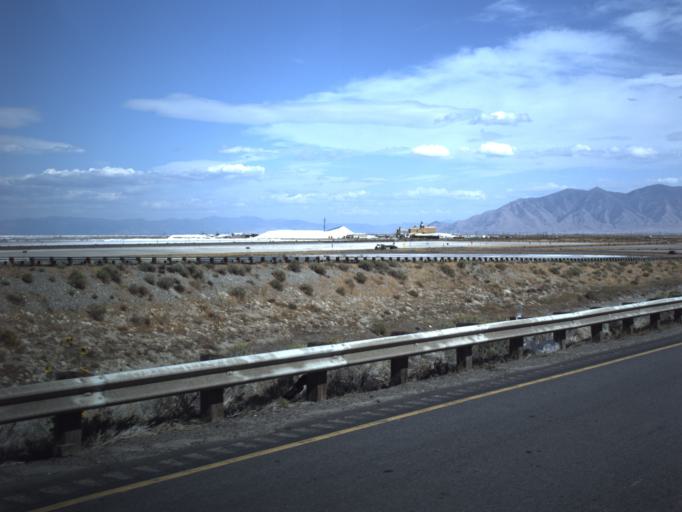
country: US
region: Utah
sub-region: Tooele County
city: Grantsville
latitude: 40.7088
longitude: -112.5288
